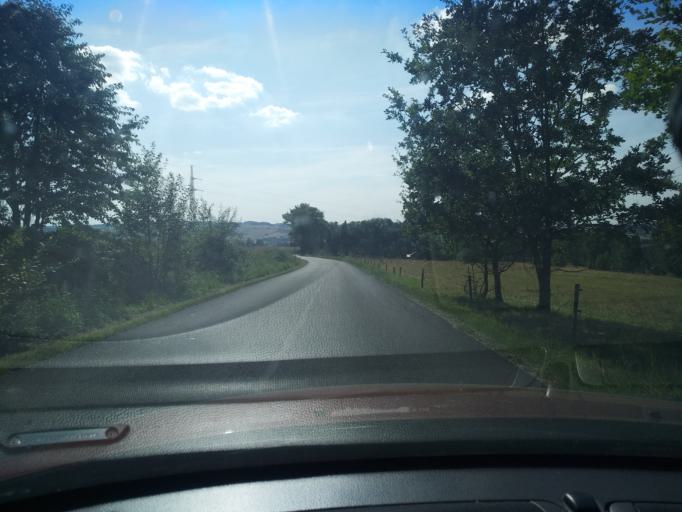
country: PL
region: Lower Silesian Voivodeship
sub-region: Powiat lubanski
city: Lesna
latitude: 51.0266
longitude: 15.2857
